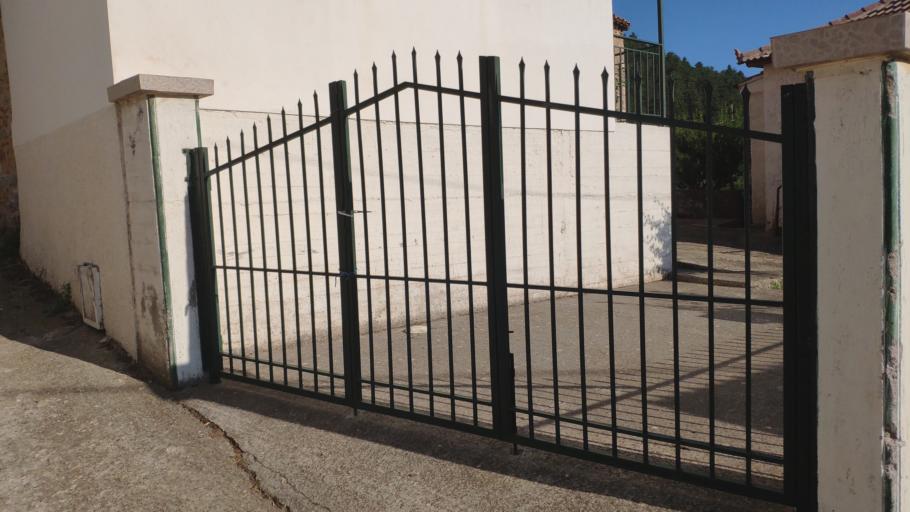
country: GR
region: Peloponnese
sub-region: Nomos Lakonias
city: Kariai
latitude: 37.1762
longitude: 22.5930
